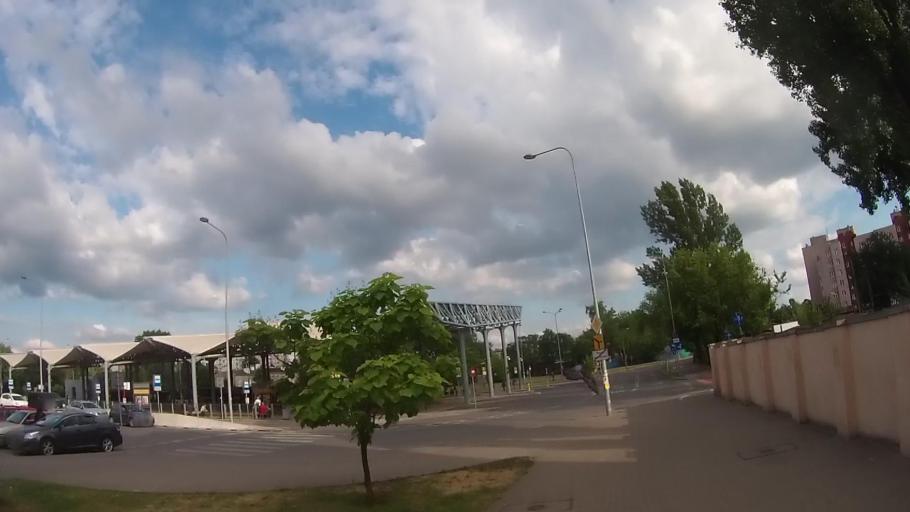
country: PL
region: Masovian Voivodeship
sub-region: Warszawa
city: Praga Polnoc
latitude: 52.2502
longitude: 21.0518
